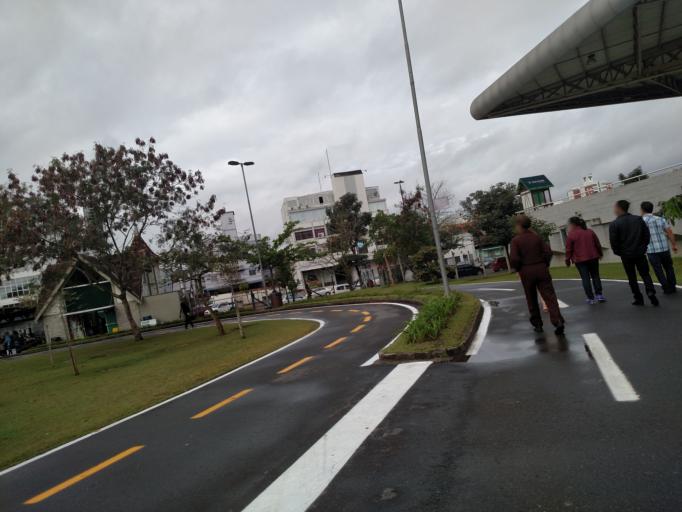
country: BR
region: Santa Catarina
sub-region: Blumenau
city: Blumenau
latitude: -26.9137
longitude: -49.0858
